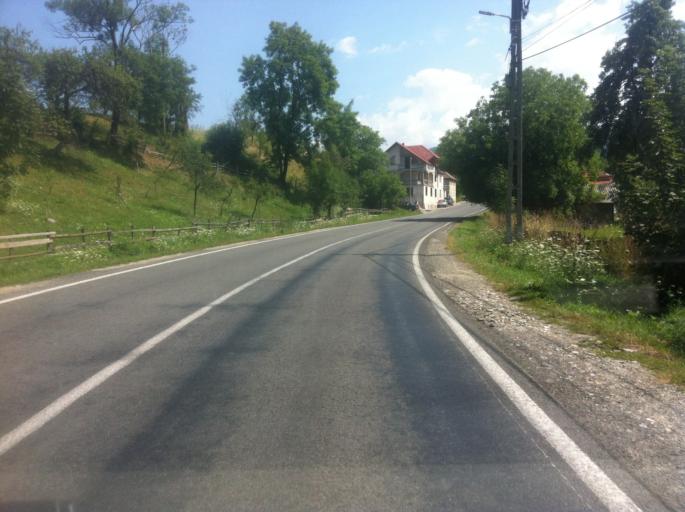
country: RO
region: Caras-Severin
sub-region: Comuna Bautar
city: Bucova
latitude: 45.5100
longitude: 22.6450
